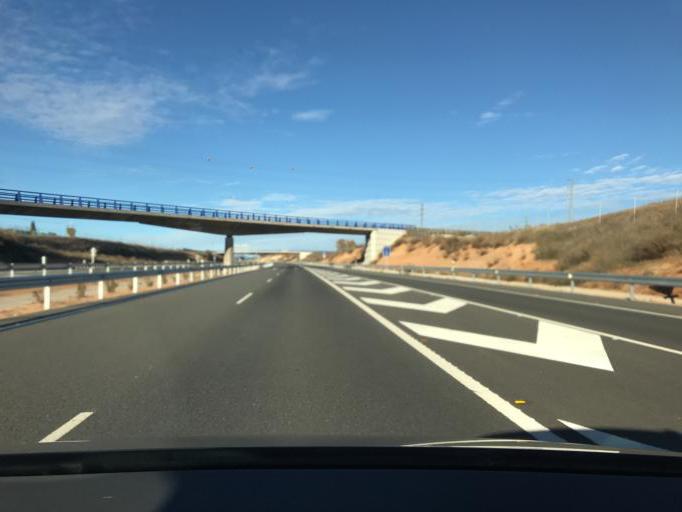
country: ES
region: Andalusia
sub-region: Provincia de Granada
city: Albolote
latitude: 37.2345
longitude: -3.6642
